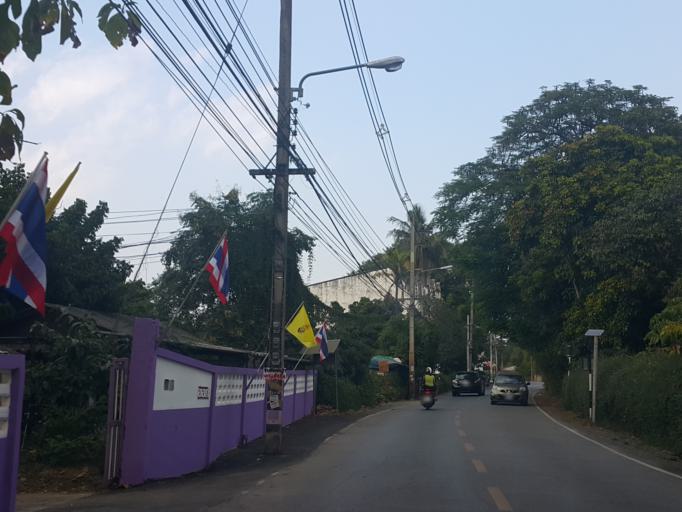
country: TH
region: Chiang Mai
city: Chiang Mai
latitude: 18.8276
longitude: 98.9949
